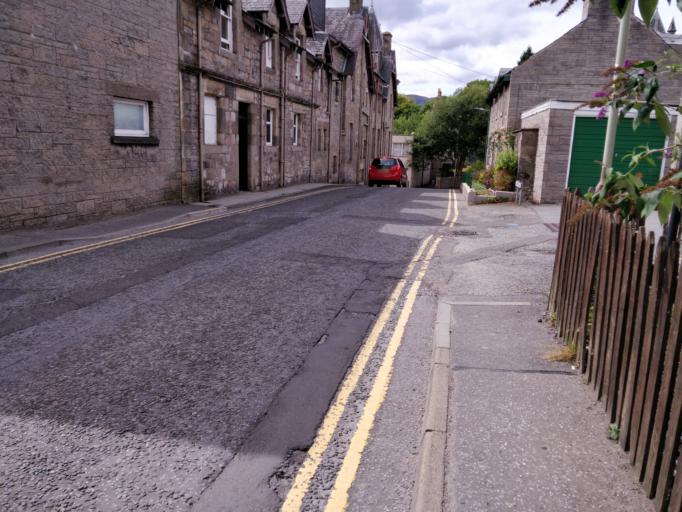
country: GB
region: Scotland
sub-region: Perth and Kinross
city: Pitlochry
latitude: 56.7036
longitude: -3.7310
